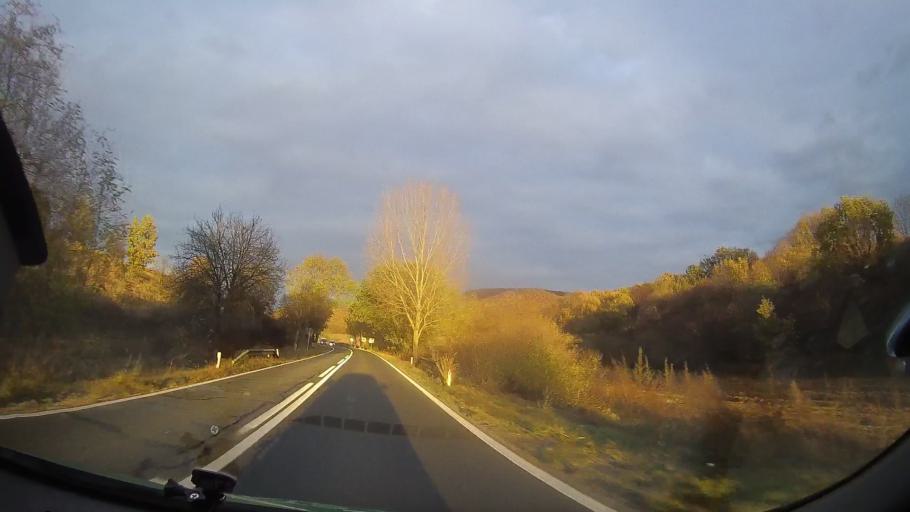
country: RO
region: Tulcea
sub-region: Comuna Ciucurova
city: Ciucurova
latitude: 44.9478
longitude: 28.5045
